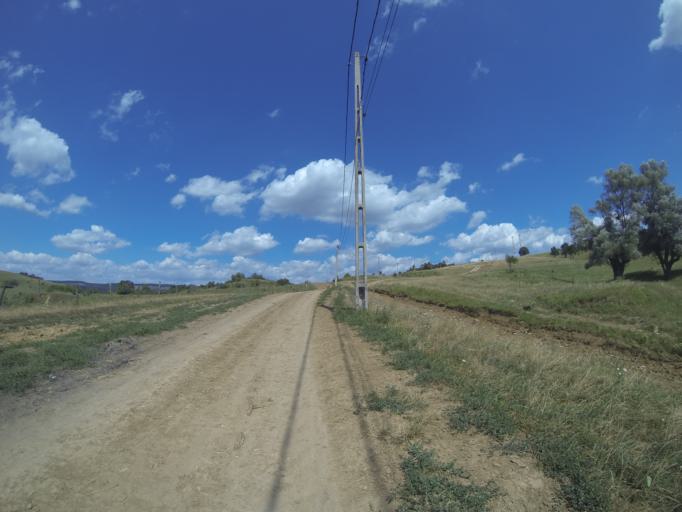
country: RO
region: Brasov
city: Fogarasch
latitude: 45.8580
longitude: 24.9858
